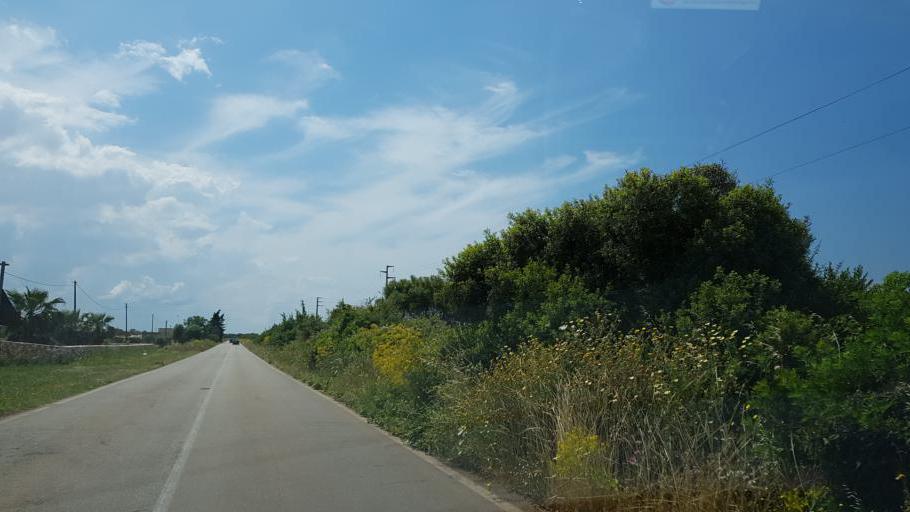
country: IT
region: Apulia
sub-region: Provincia di Lecce
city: Porto Cesareo
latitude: 40.3241
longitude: 17.8549
